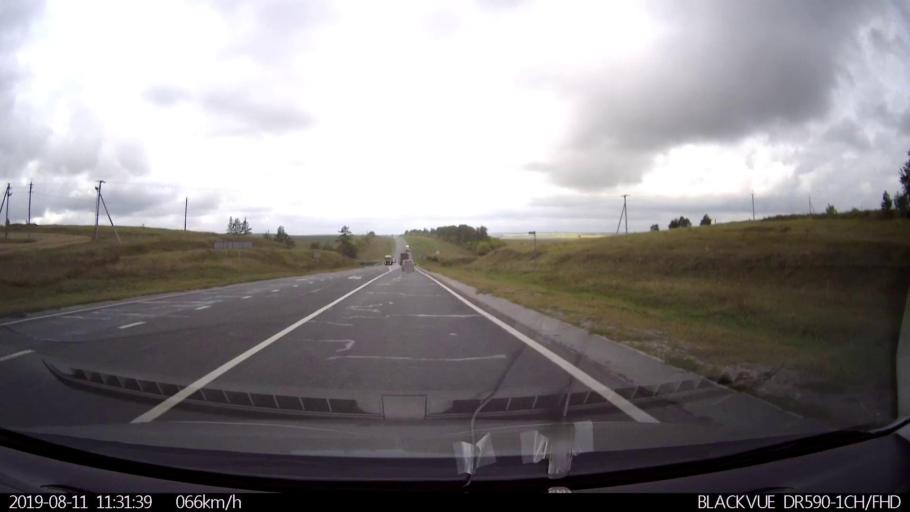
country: RU
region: Ulyanovsk
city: Krasnyy Gulyay
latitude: 54.0458
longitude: 48.2155
